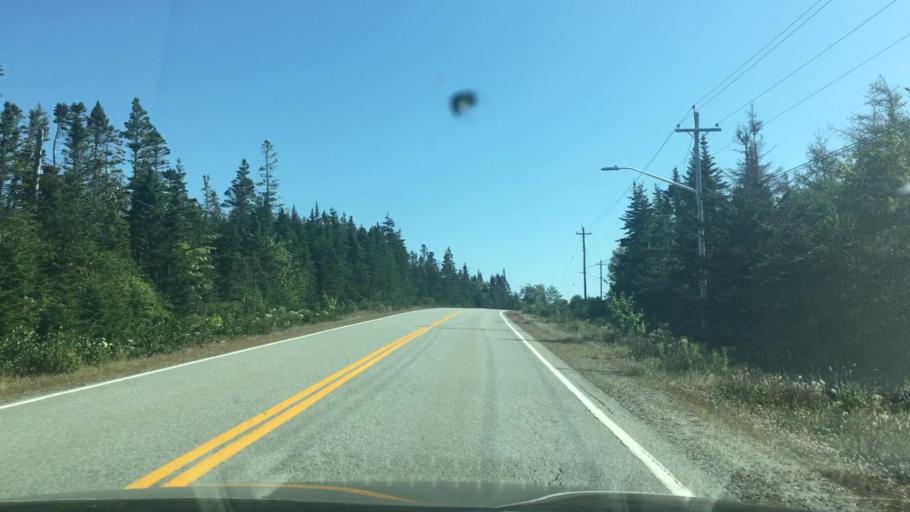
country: CA
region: Nova Scotia
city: Cole Harbour
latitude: 44.7783
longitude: -62.7831
